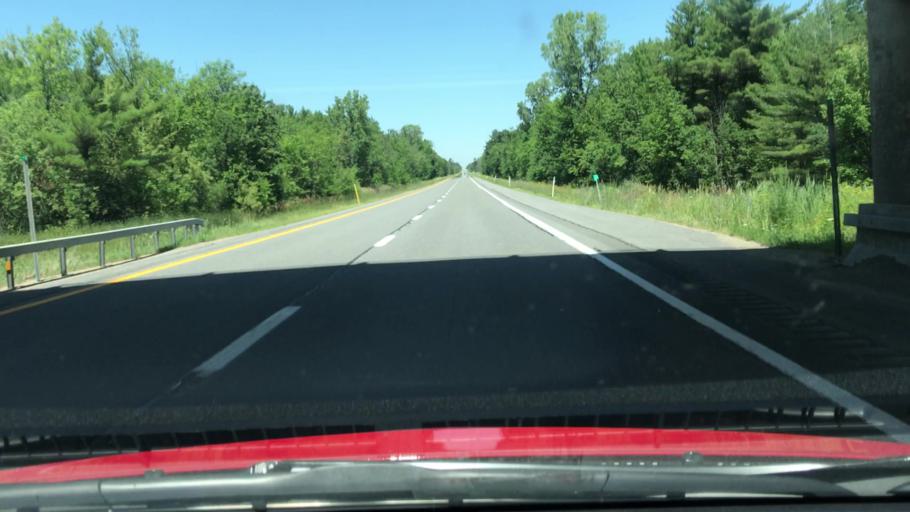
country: US
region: New York
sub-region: Clinton County
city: Champlain
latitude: 44.9316
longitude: -73.4463
